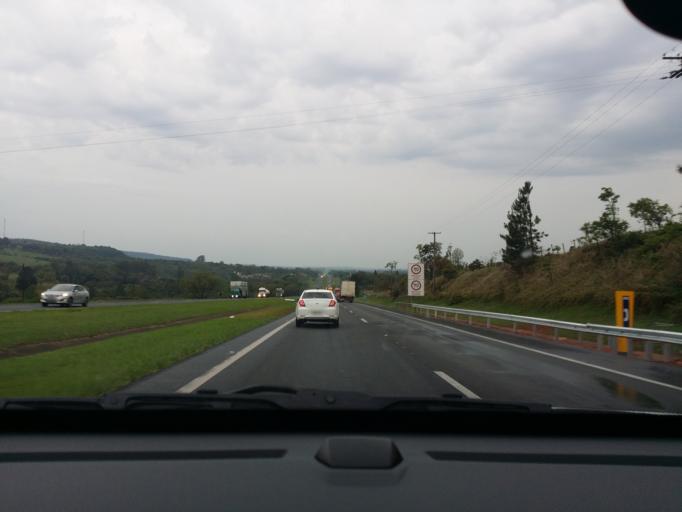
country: BR
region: Sao Paulo
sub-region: Sao Carlos
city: Sao Carlos
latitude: -22.0581
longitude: -47.8537
